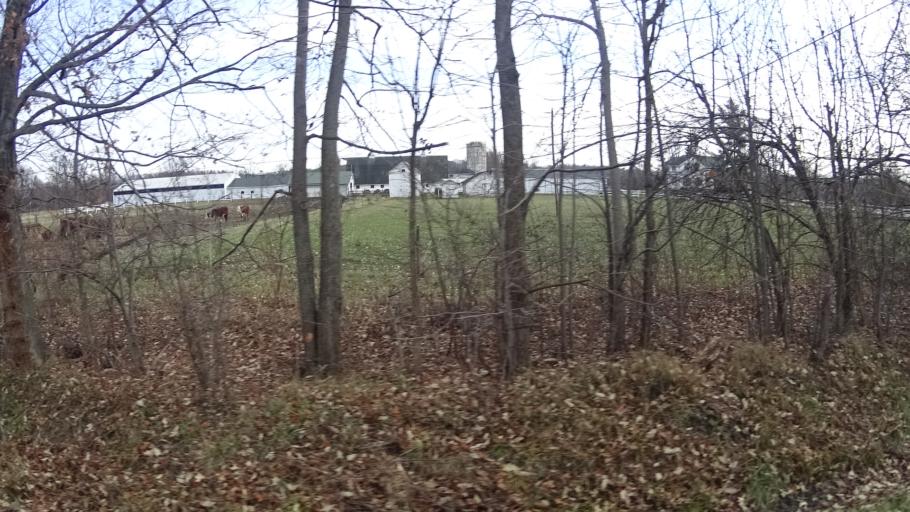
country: US
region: Ohio
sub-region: Lorain County
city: Eaton Estates
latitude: 41.2511
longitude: -81.9730
